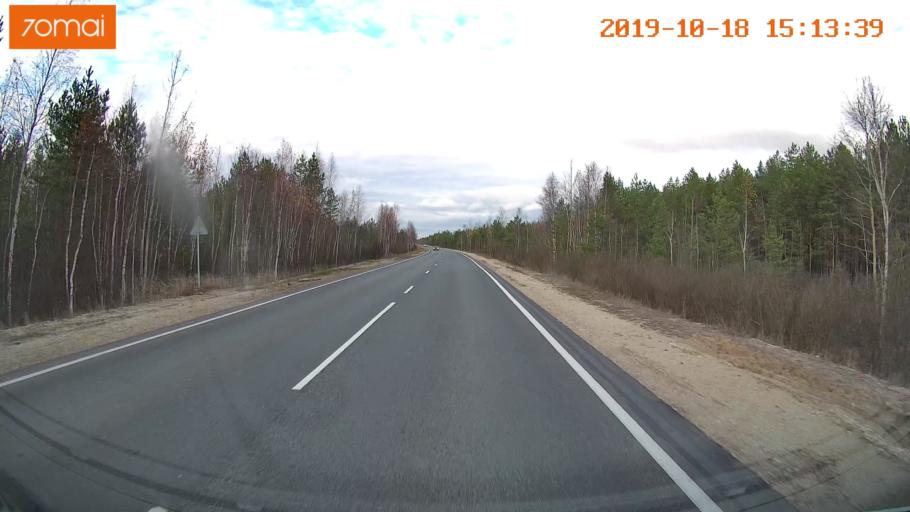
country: RU
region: Vladimir
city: Gus'-Khrustal'nyy
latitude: 55.5900
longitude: 40.7187
